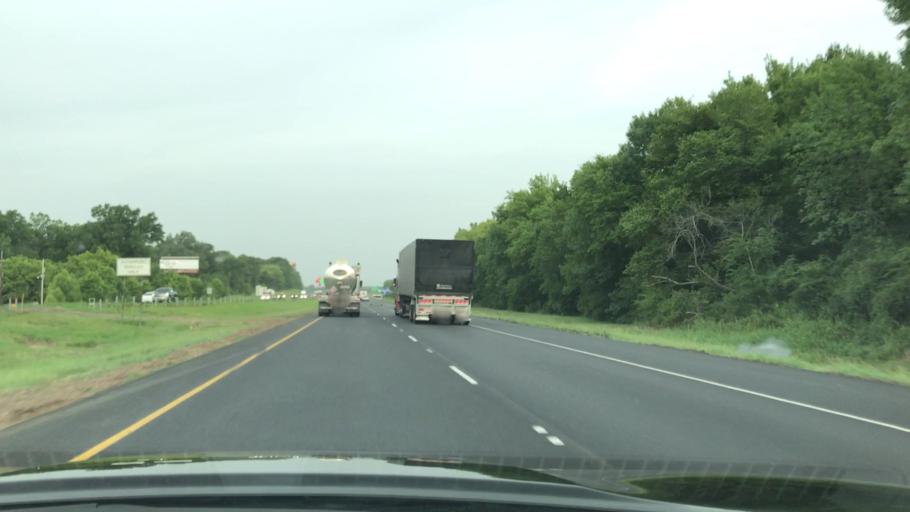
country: US
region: Louisiana
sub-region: Caddo Parish
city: Greenwood
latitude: 32.4459
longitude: -93.9679
